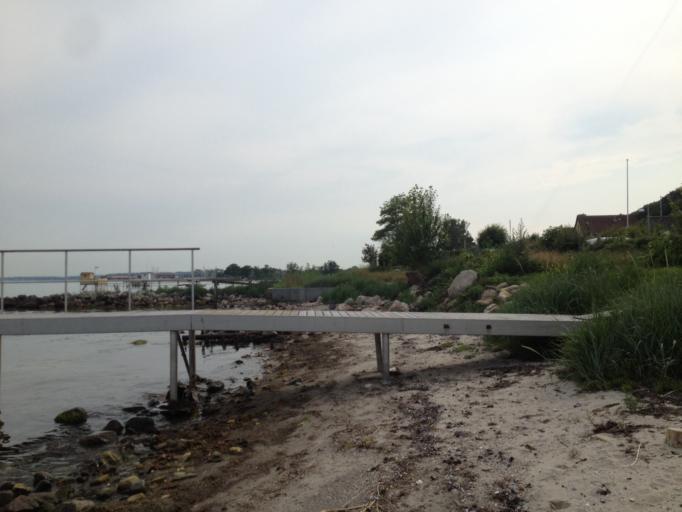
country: DK
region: Capital Region
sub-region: Fredensborg Kommune
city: Humlebaek
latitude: 55.9467
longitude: 12.5298
